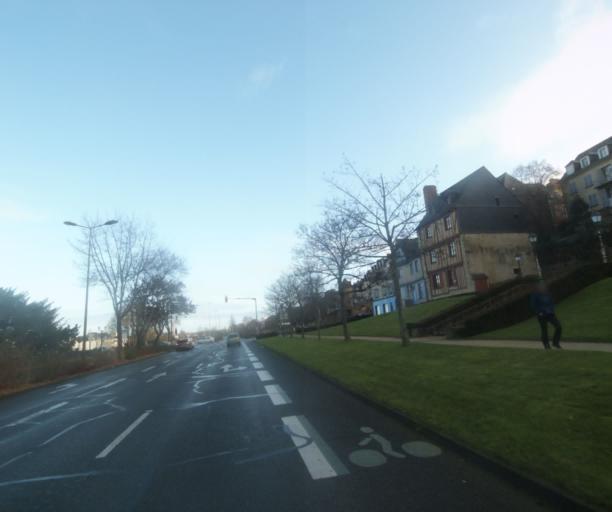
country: FR
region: Pays de la Loire
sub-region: Departement de la Sarthe
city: Le Mans
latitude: 48.0088
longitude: 0.1949
